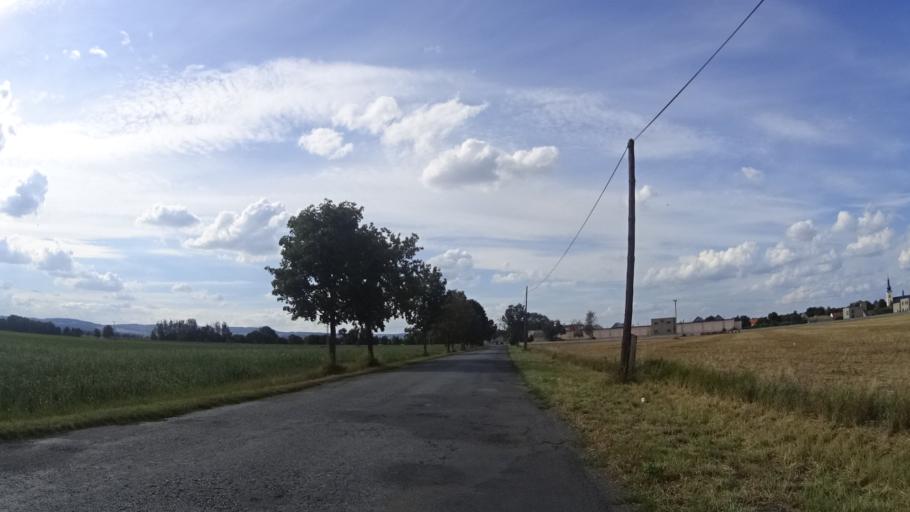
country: CZ
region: Olomoucky
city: Moravicany
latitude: 49.7507
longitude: 16.9695
